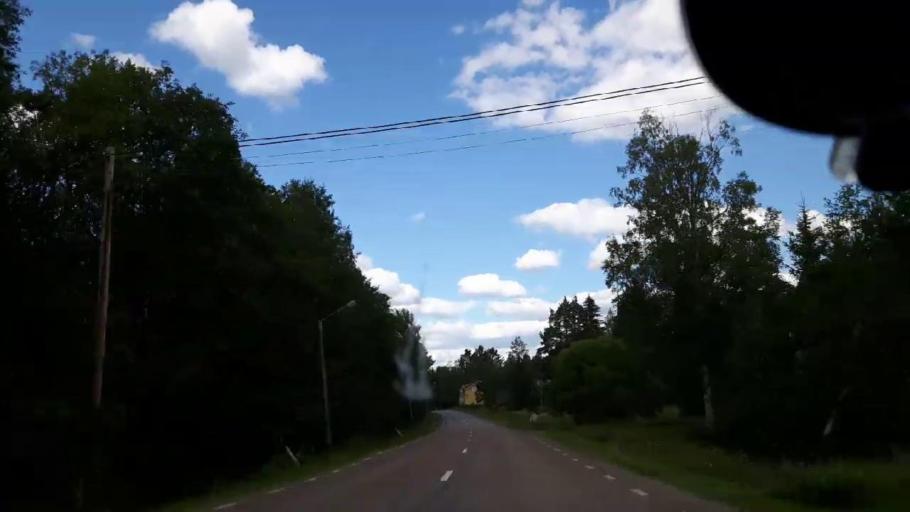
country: SE
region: Jaemtland
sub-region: Ragunda Kommun
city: Hammarstrand
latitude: 62.9973
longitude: 16.6769
